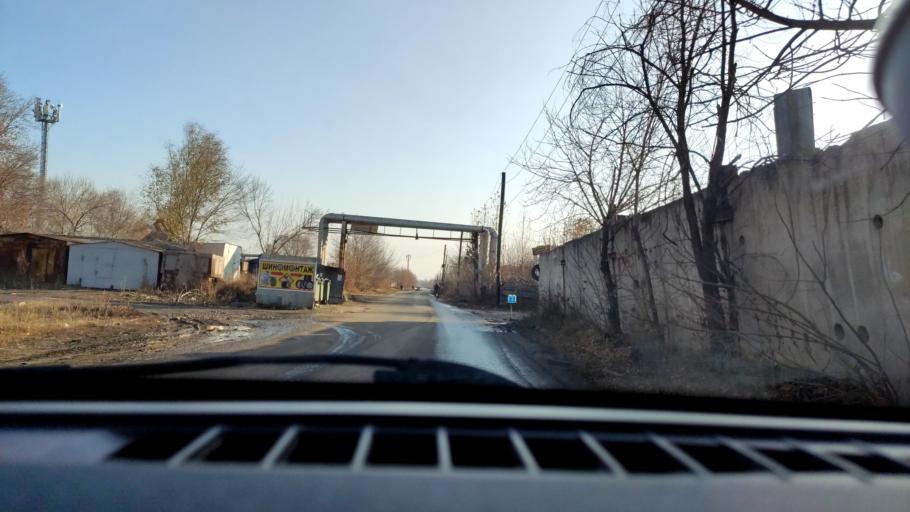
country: RU
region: Samara
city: Samara
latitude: 53.1198
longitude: 50.0956
